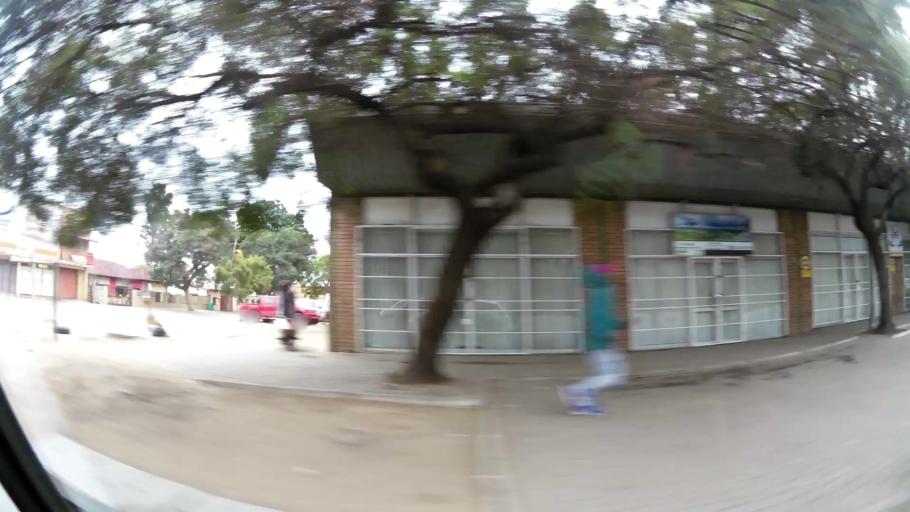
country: ZA
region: Limpopo
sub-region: Capricorn District Municipality
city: Polokwane
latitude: -23.9062
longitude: 29.4441
